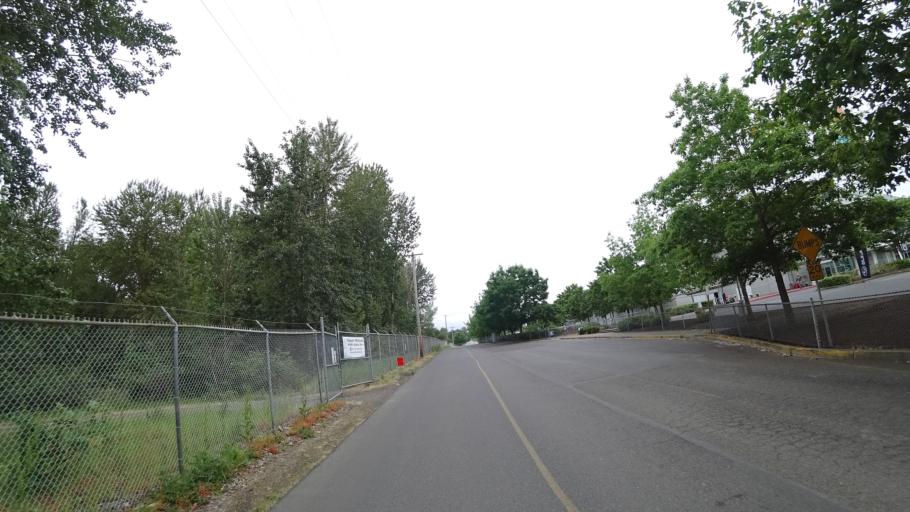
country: US
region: Washington
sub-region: Clark County
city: Vancouver
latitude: 45.6051
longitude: -122.6895
